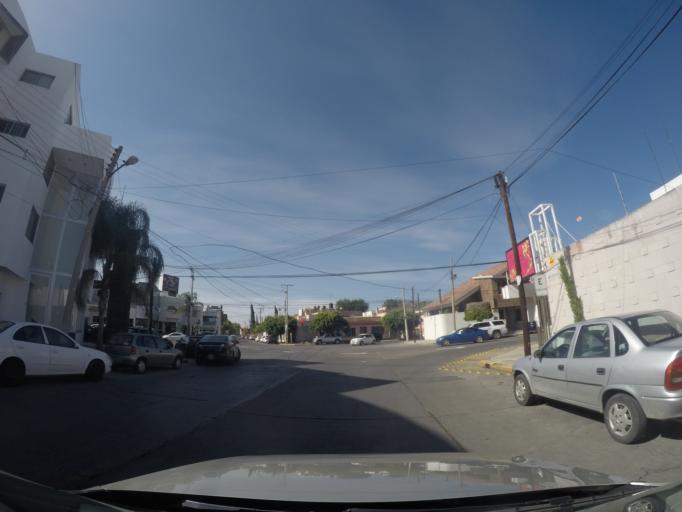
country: MX
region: San Luis Potosi
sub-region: San Luis Potosi
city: San Luis Potosi
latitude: 22.1473
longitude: -101.0038
